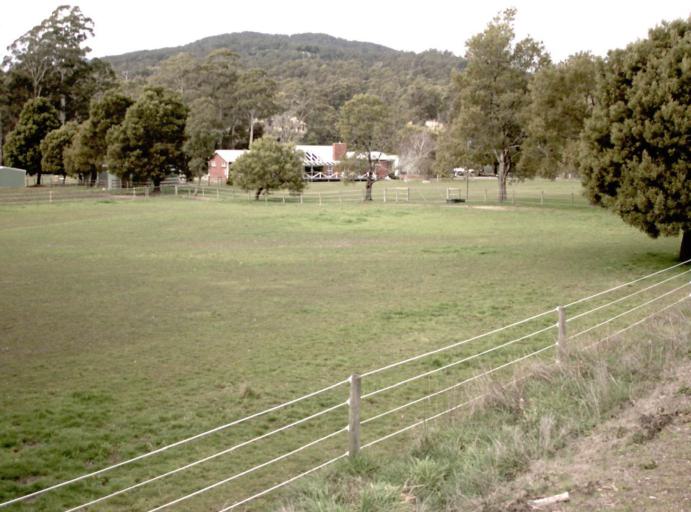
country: AU
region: Tasmania
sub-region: Launceston
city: Mayfield
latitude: -41.2626
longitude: 147.1602
